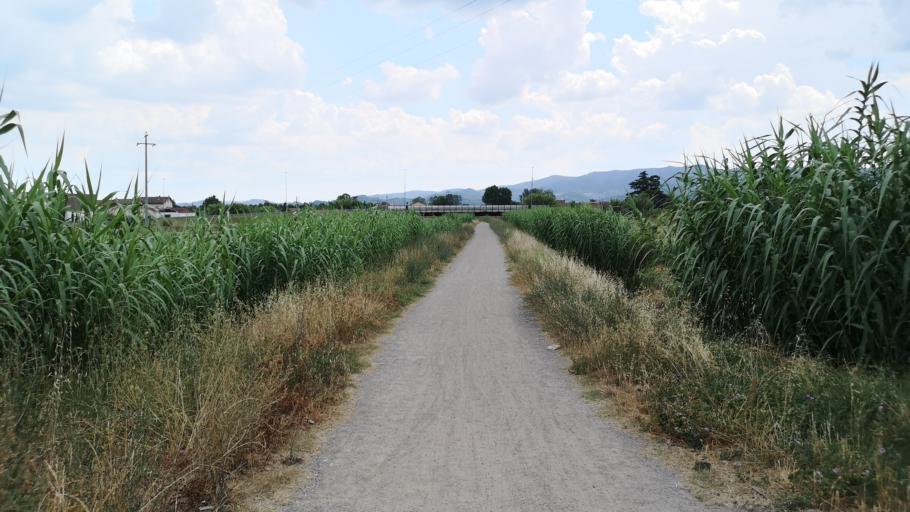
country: IT
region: Tuscany
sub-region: Provincia di Prato
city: Fornacelle
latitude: 43.8805
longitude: 11.0480
